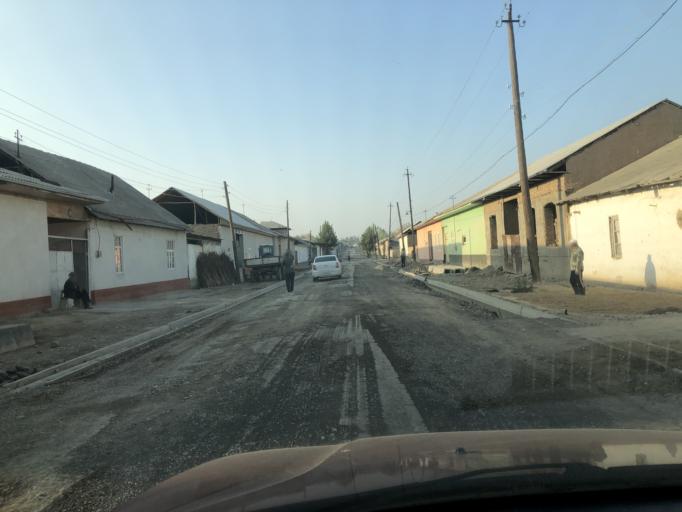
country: UZ
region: Namangan
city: Uychi
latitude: 41.0782
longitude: 72.0017
